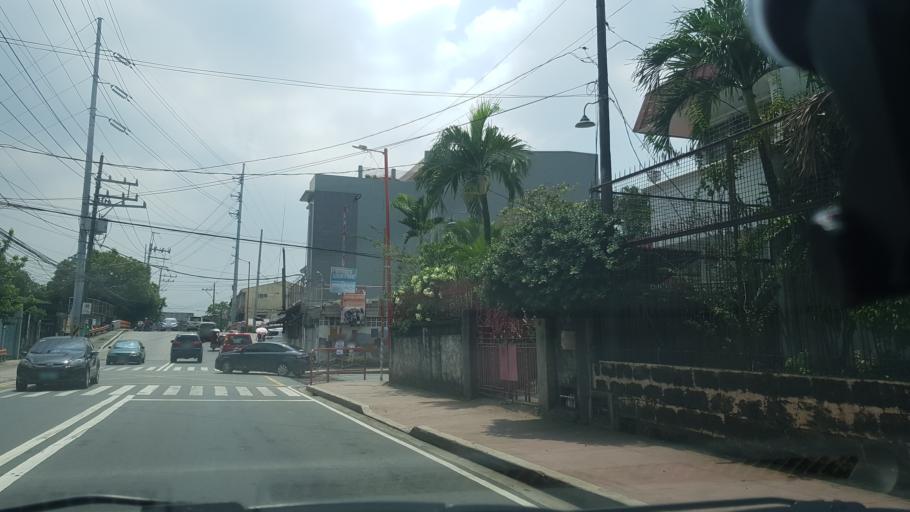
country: PH
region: Calabarzon
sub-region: Province of Rizal
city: Antipolo
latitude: 14.6373
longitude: 121.1215
